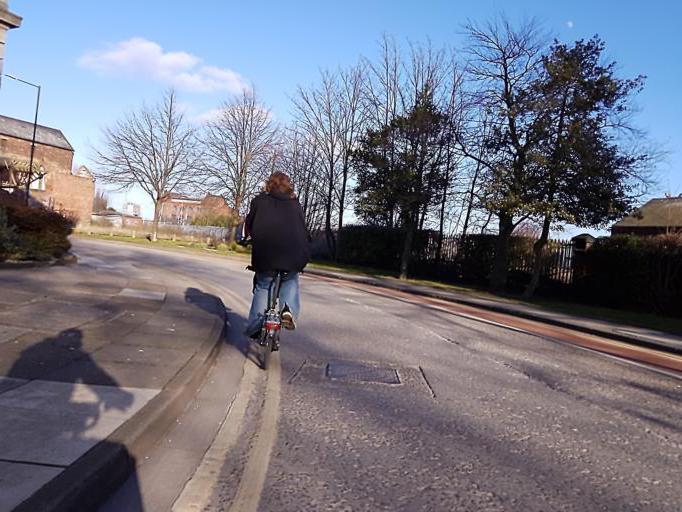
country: GB
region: England
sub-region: North East Lincolnshire
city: Grimsby
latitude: 53.5650
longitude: -0.0812
